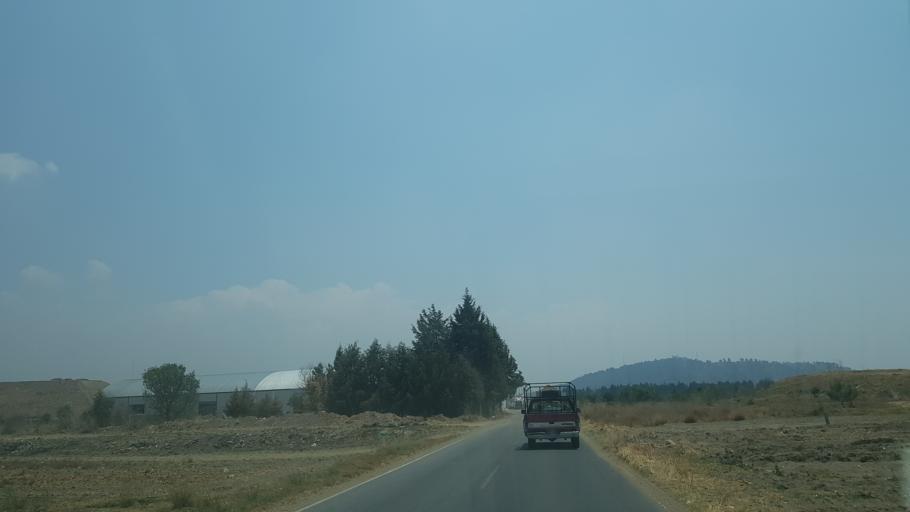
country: MX
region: Puebla
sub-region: San Jeronimo Tecuanipan
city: San Miguel Papaxtla
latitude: 19.0904
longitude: -98.3838
